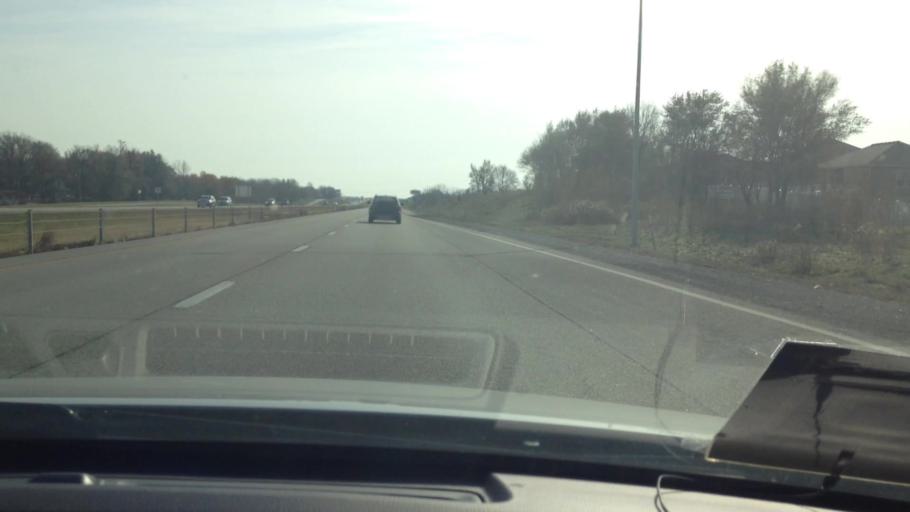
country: US
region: Missouri
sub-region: Cass County
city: Peculiar
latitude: 38.7197
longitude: -94.4521
